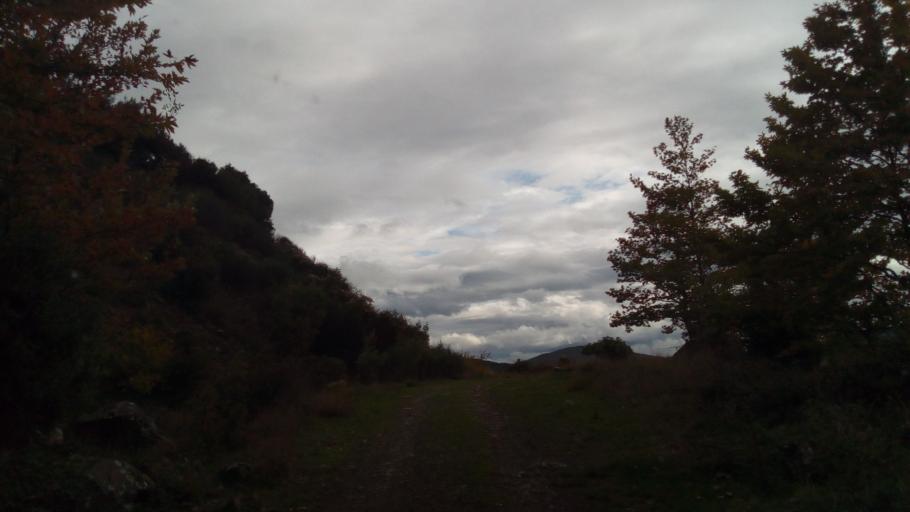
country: GR
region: West Greece
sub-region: Nomos Aitolias kai Akarnanias
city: Nafpaktos
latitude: 38.5639
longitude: 21.9569
